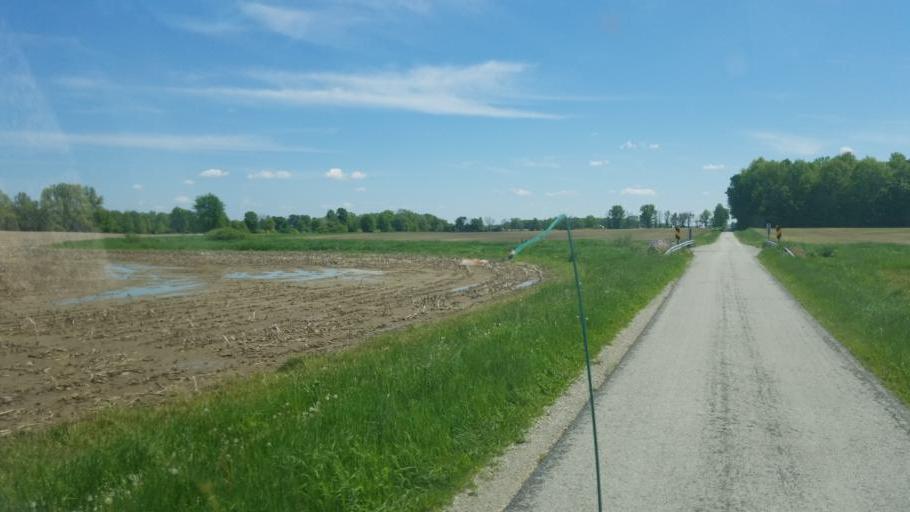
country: US
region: Ohio
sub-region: Huron County
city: Willard
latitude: 41.0469
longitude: -82.9390
